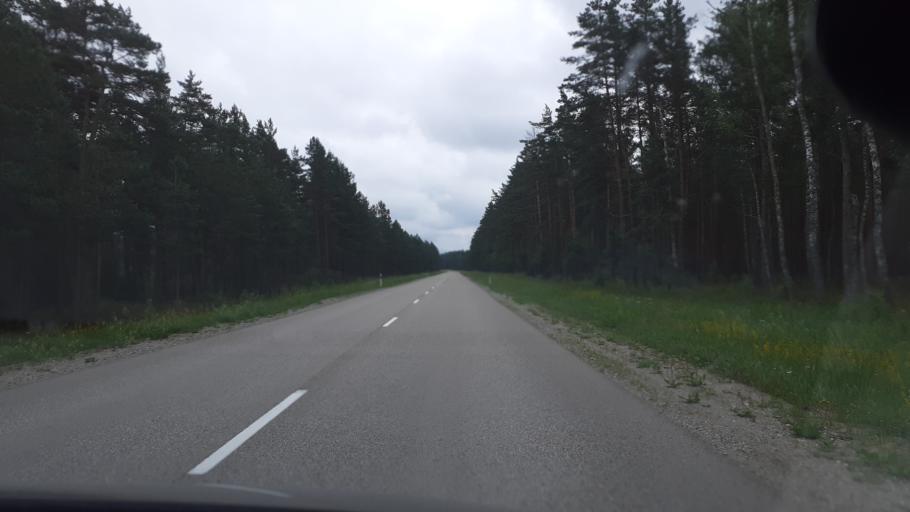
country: LV
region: Ventspils Rajons
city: Piltene
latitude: 57.1245
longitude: 21.7394
